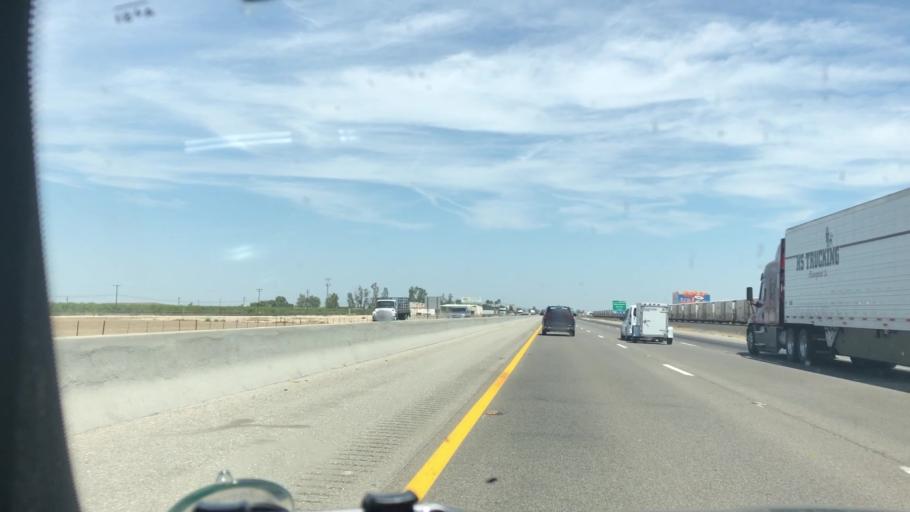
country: US
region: California
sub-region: Kern County
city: Delano
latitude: 35.7272
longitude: -119.2386
